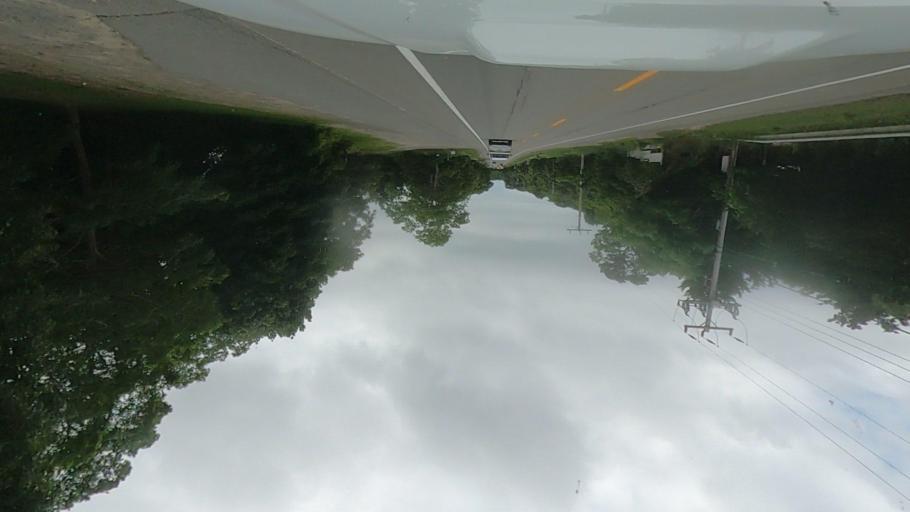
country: US
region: Massachusetts
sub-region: Barnstable County
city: Wellfleet
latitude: 41.9249
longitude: -70.0119
